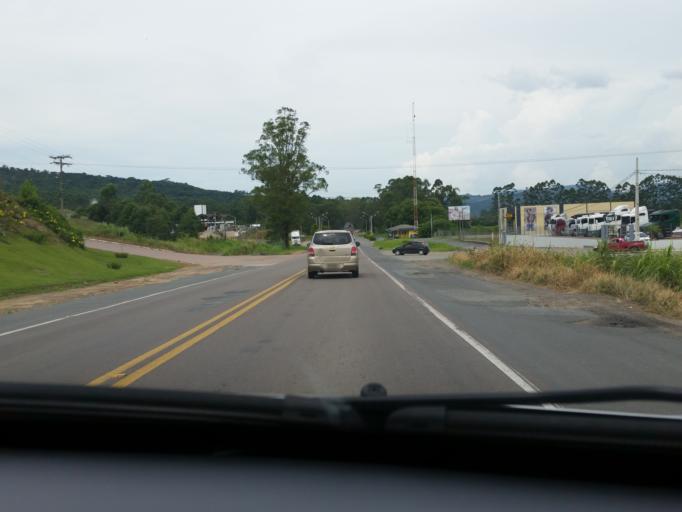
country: BR
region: Santa Catarina
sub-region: Rio Do Sul
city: Rio do Sul
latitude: -27.1728
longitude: -49.5840
